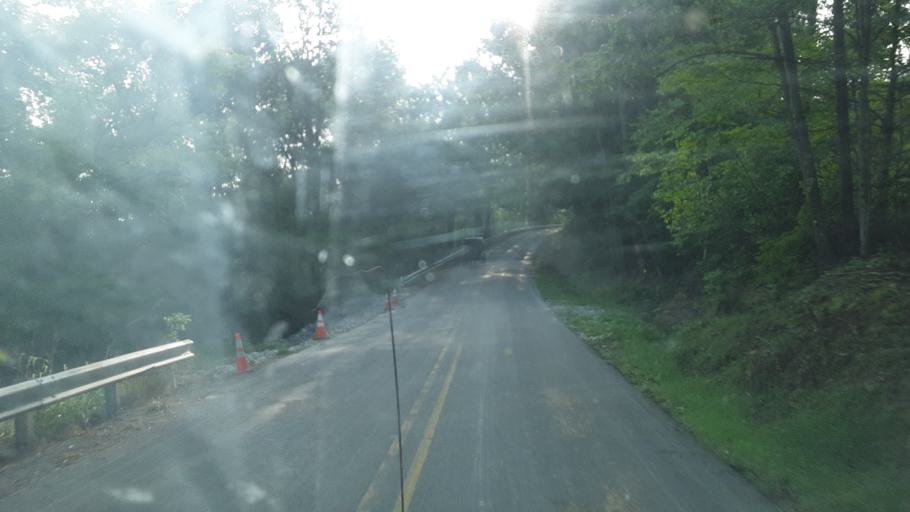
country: US
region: Pennsylvania
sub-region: Jefferson County
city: Punxsutawney
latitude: 40.9521
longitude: -79.1376
